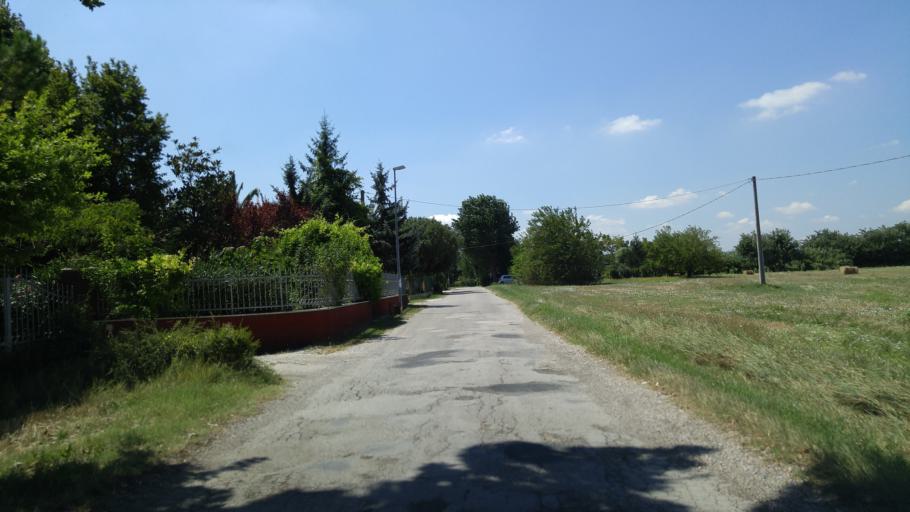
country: IT
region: The Marches
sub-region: Provincia di Pesaro e Urbino
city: Cuccurano
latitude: 43.7960
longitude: 12.9690
